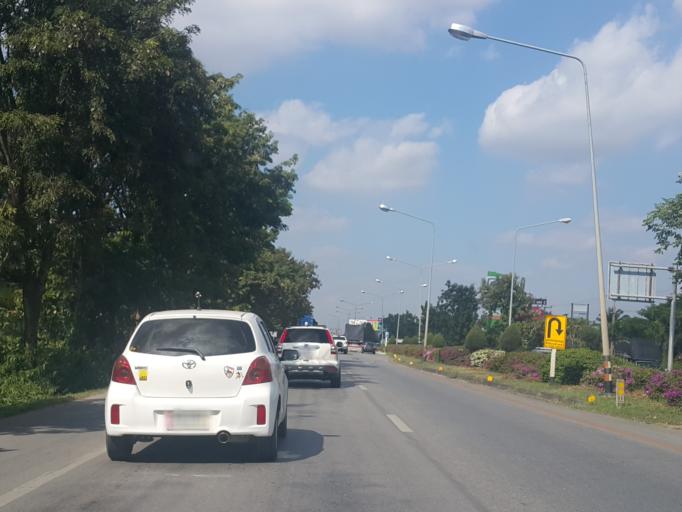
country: TH
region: Chiang Mai
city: Saraphi
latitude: 18.7450
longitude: 99.0345
